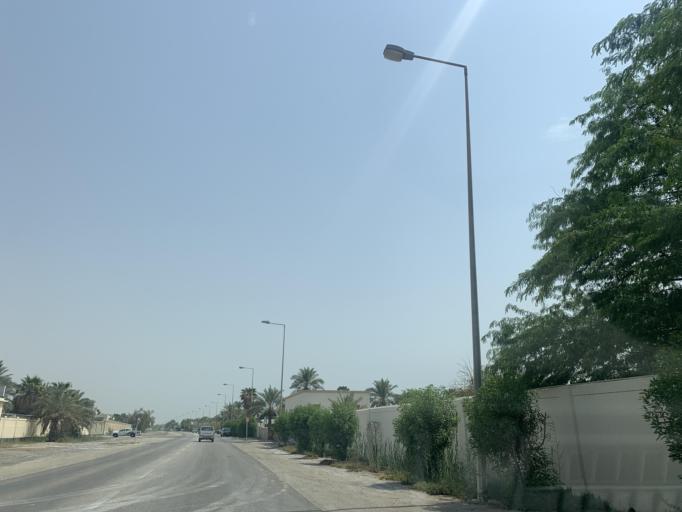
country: BH
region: Central Governorate
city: Madinat Hamad
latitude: 26.1651
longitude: 50.4653
